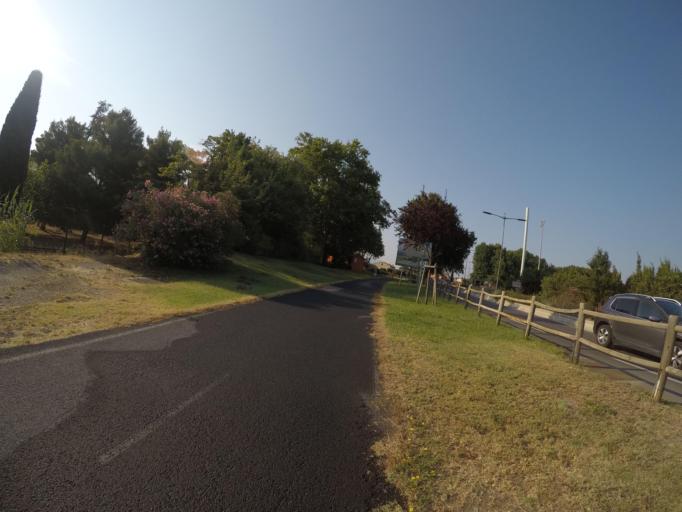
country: FR
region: Languedoc-Roussillon
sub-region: Departement des Pyrenees-Orientales
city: Canohes
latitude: 42.6593
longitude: 2.8348
